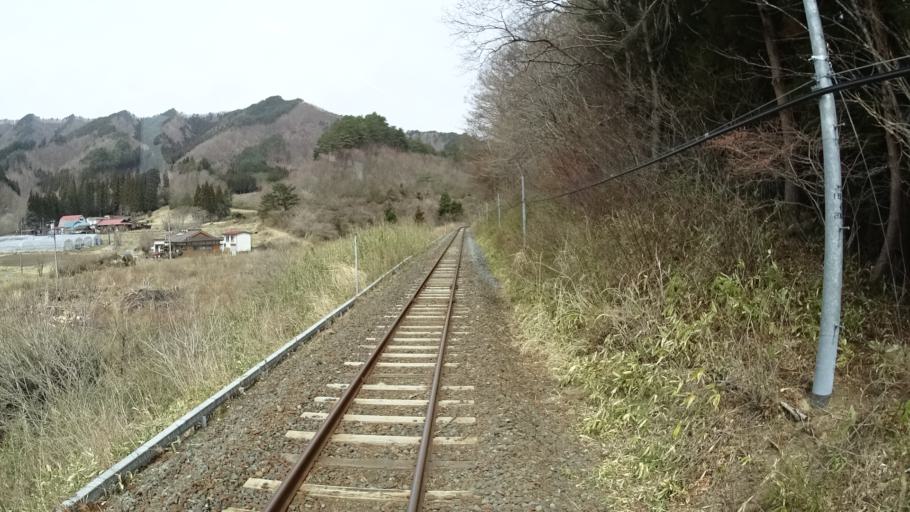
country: JP
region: Iwate
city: Yamada
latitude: 39.4885
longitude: 141.9241
